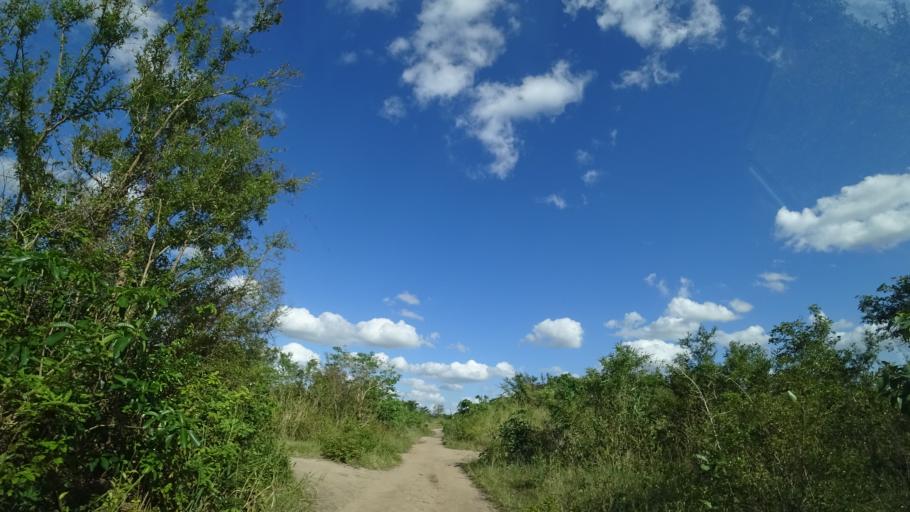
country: MZ
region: Sofala
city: Dondo
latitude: -19.4265
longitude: 34.7238
